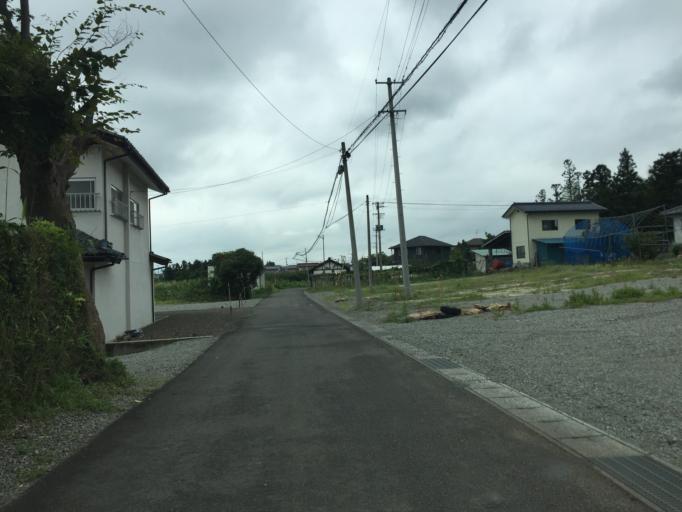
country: JP
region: Fukushima
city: Fukushima-shi
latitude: 37.8055
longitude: 140.4031
